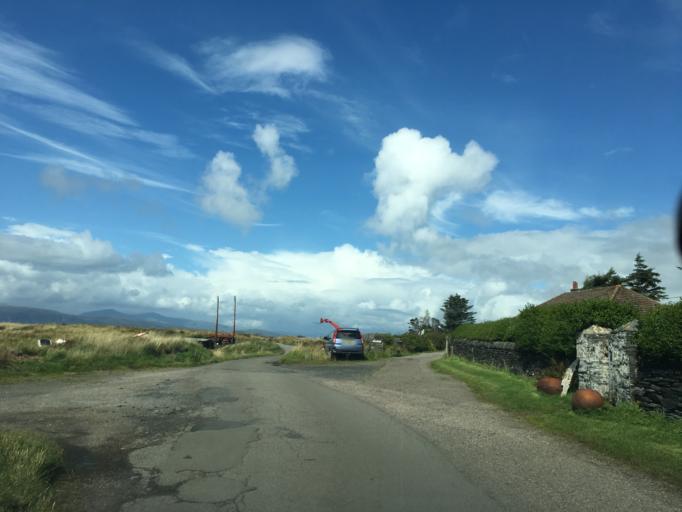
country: GB
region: Scotland
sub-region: Argyll and Bute
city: Isle Of Mull
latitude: 56.2518
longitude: -5.6540
